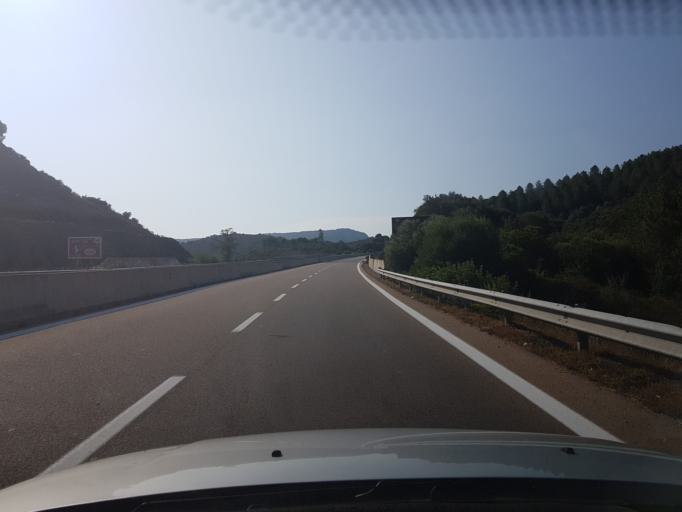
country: IT
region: Sardinia
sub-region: Provincia di Olbia-Tempio
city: Loiri Porto San Paolo
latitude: 40.8272
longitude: 9.5771
